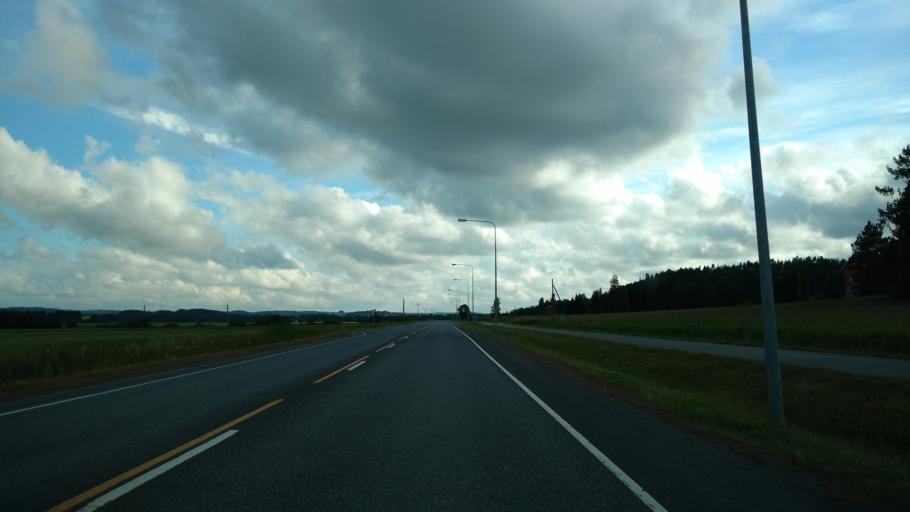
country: FI
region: Varsinais-Suomi
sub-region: Salo
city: Salo
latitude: 60.4140
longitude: 23.1616
